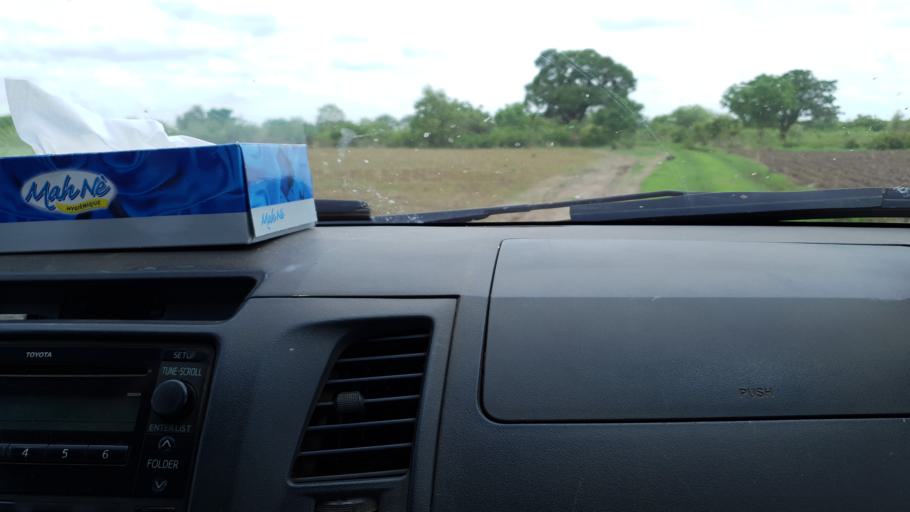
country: ML
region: Segou
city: Baroueli
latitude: 13.3466
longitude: -7.0938
